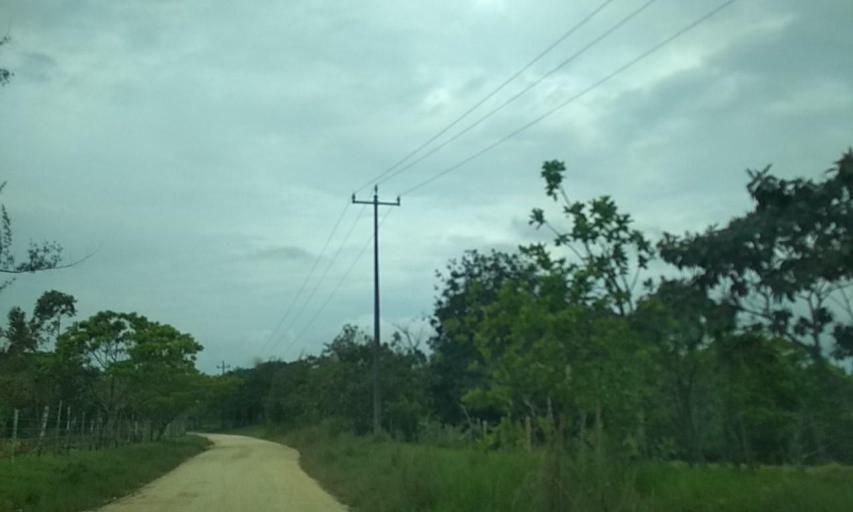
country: MX
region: Veracruz
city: Las Choapas
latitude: 17.8844
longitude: -94.1266
